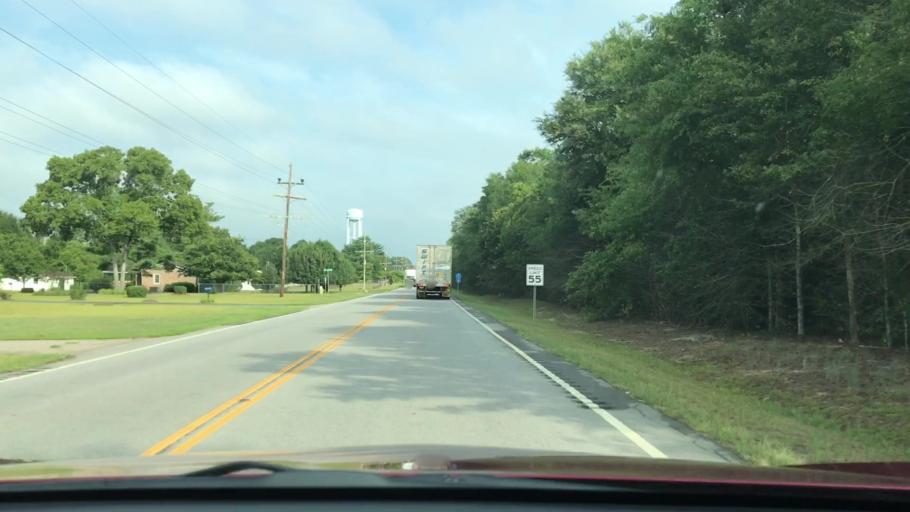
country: US
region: South Carolina
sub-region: Barnwell County
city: Williston
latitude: 33.6369
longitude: -81.3246
